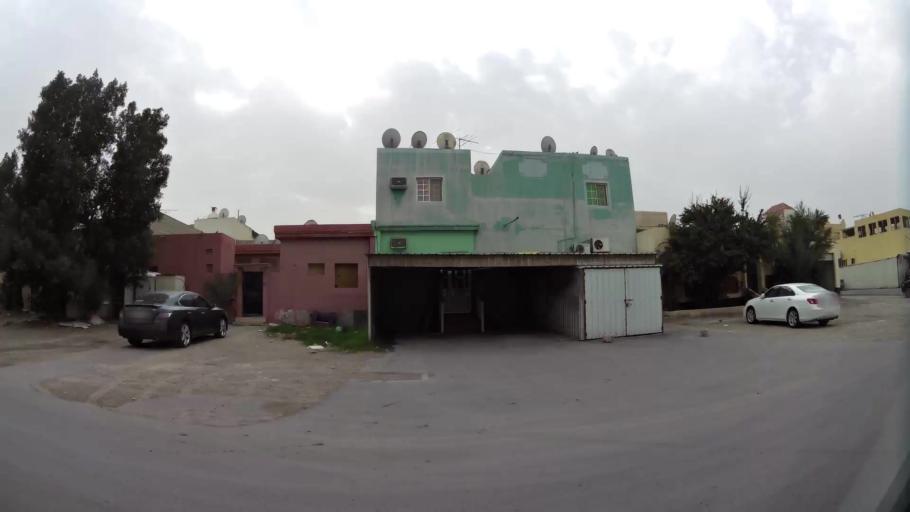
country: BH
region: Northern
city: Ar Rifa'
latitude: 26.1271
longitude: 50.5788
